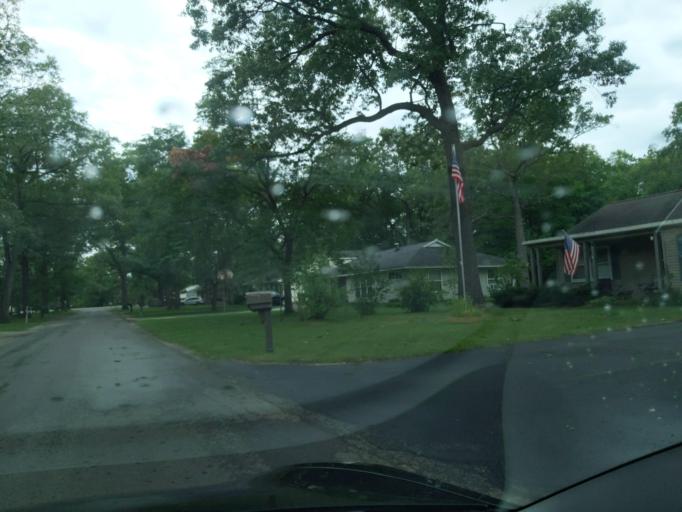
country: US
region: Michigan
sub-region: Grand Traverse County
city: Traverse City
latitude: 44.7509
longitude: -85.5725
